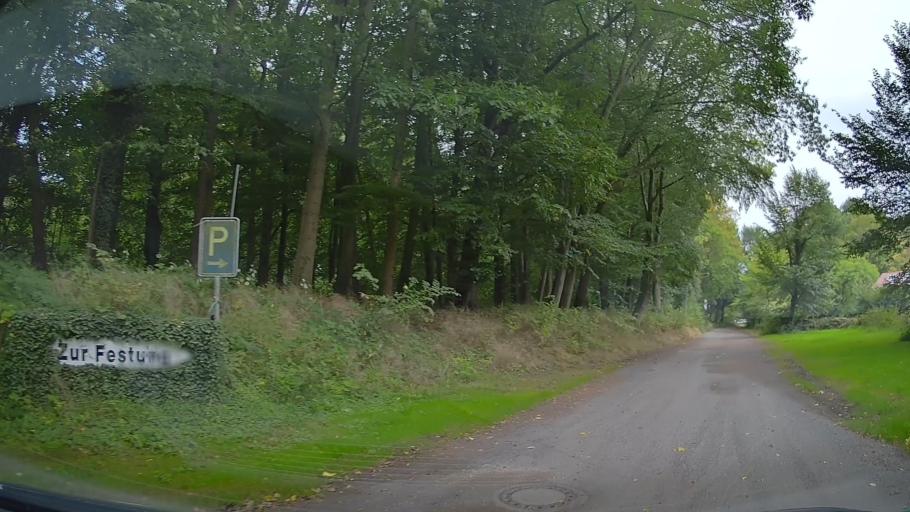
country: DE
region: Schleswig-Holstein
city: Kollmar
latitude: 53.6779
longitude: 9.4879
